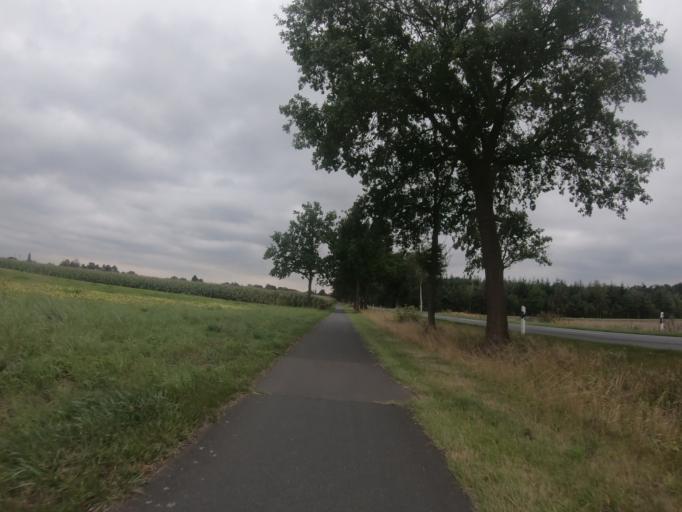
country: DE
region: Lower Saxony
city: Ribbesbuttel
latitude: 52.4386
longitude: 10.5046
